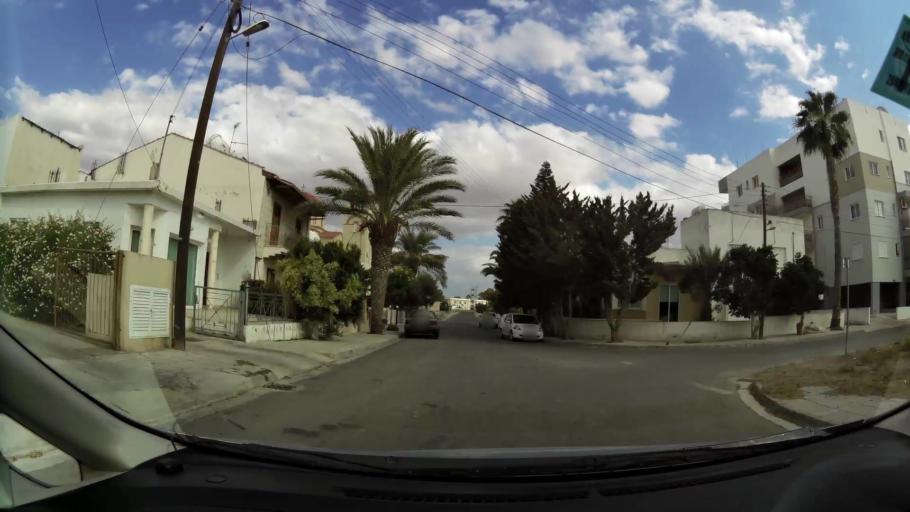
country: CY
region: Lefkosia
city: Nicosia
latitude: 35.1884
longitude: 33.3911
